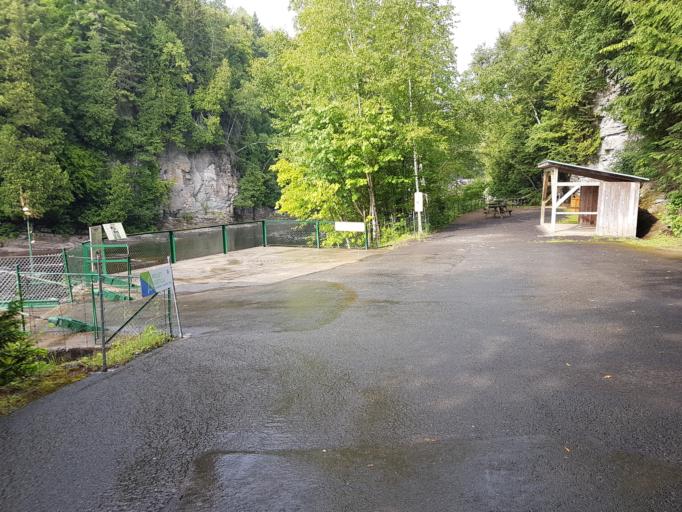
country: CA
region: Quebec
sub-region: Capitale-Nationale
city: Beaupre
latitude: 47.0746
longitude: -70.8751
